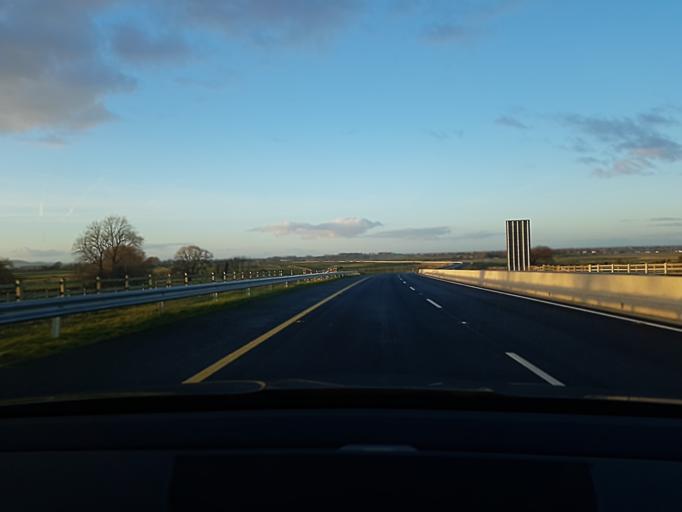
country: IE
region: Connaught
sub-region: County Galway
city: Tuam
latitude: 53.4145
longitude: -8.8288
